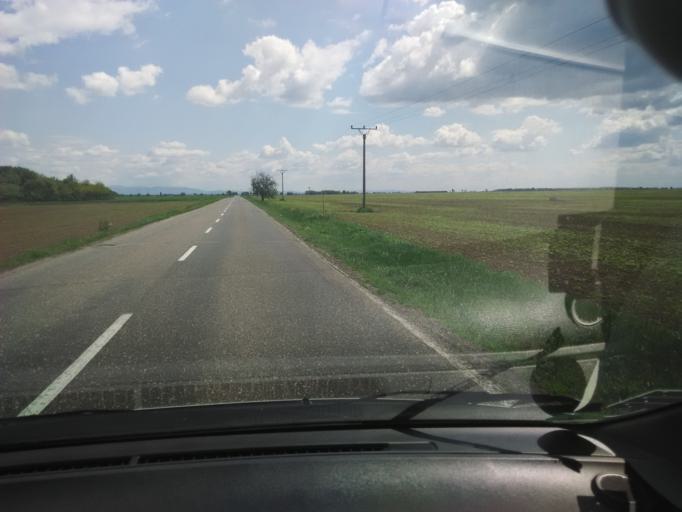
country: SK
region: Nitriansky
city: Levice
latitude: 48.1804
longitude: 18.5262
